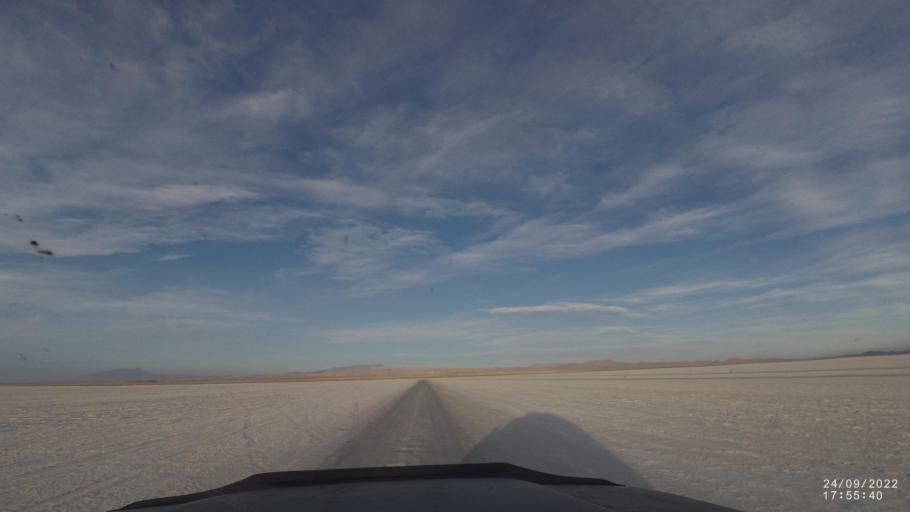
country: BO
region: Potosi
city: Colchani
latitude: -20.3268
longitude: -67.0271
